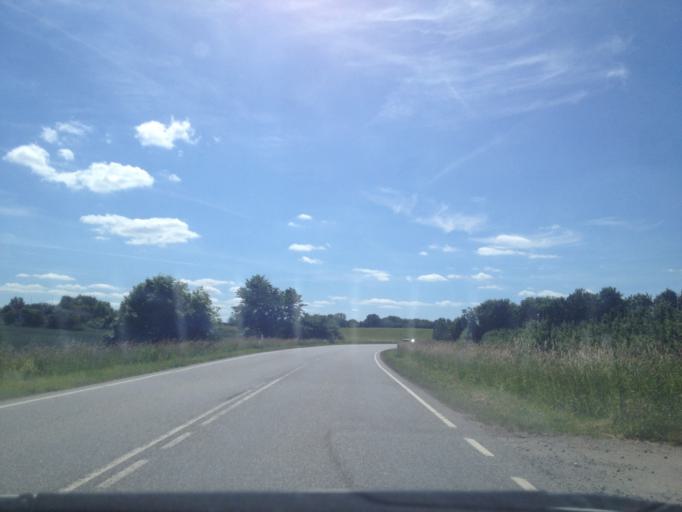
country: DK
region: Zealand
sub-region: Odsherred Kommune
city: Horve
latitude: 55.7542
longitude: 11.3778
